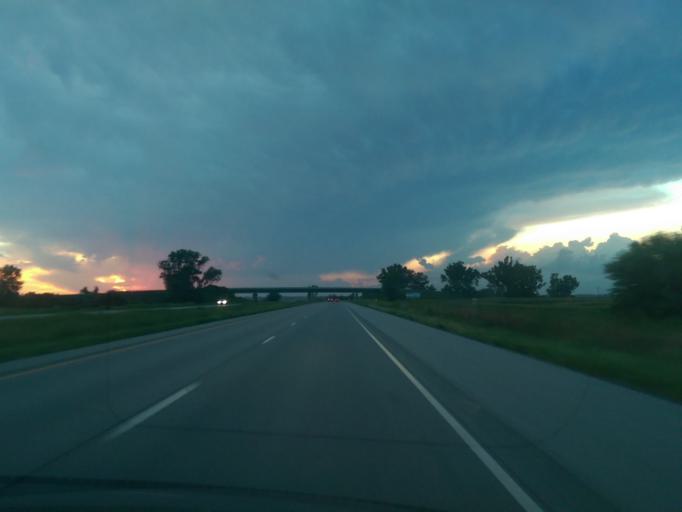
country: US
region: Nebraska
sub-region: Otoe County
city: Nebraska City
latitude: 40.7213
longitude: -95.8097
